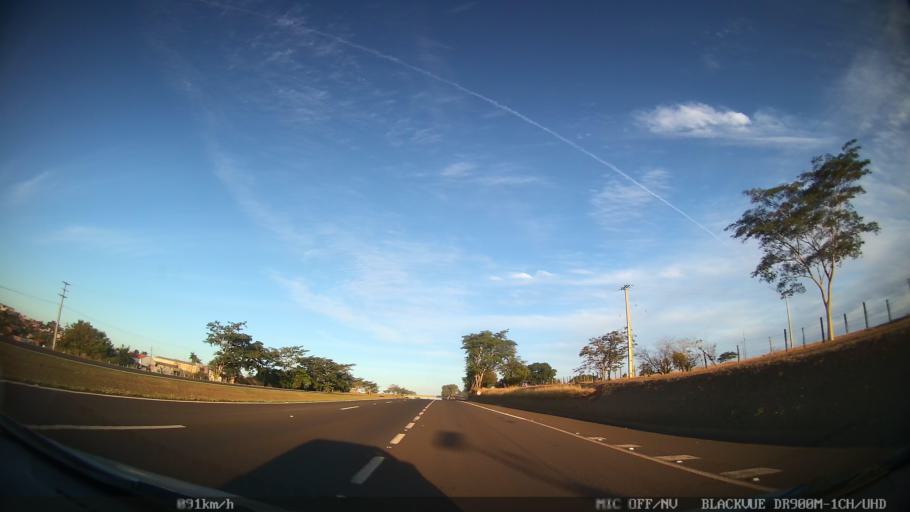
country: BR
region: Sao Paulo
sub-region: Catanduva
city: Catanduva
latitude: -21.1312
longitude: -49.0242
